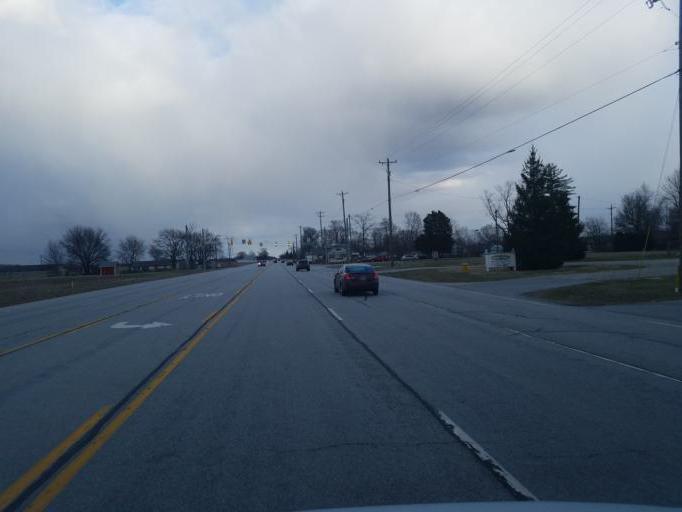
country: US
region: Indiana
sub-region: Hancock County
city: New Palestine
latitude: 39.7793
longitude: -85.8982
